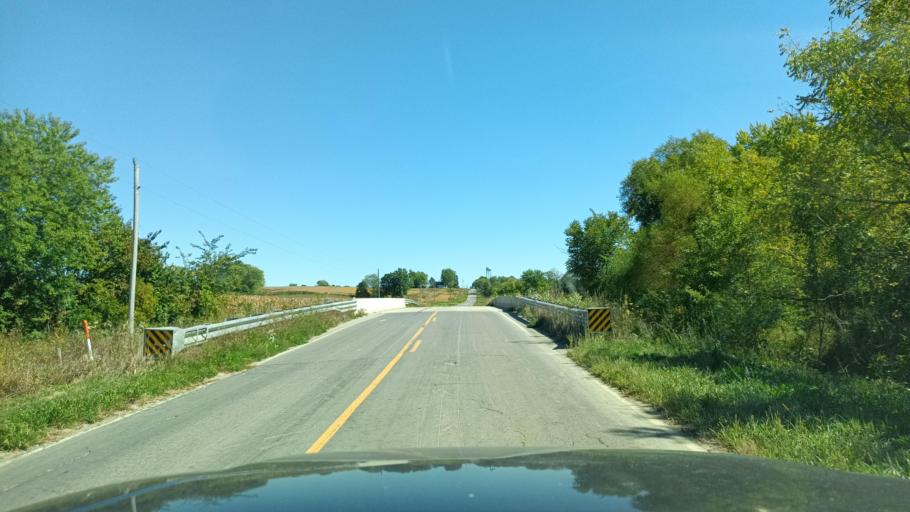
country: US
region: Missouri
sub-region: Macon County
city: La Plata
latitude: 40.0220
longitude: -92.5427
